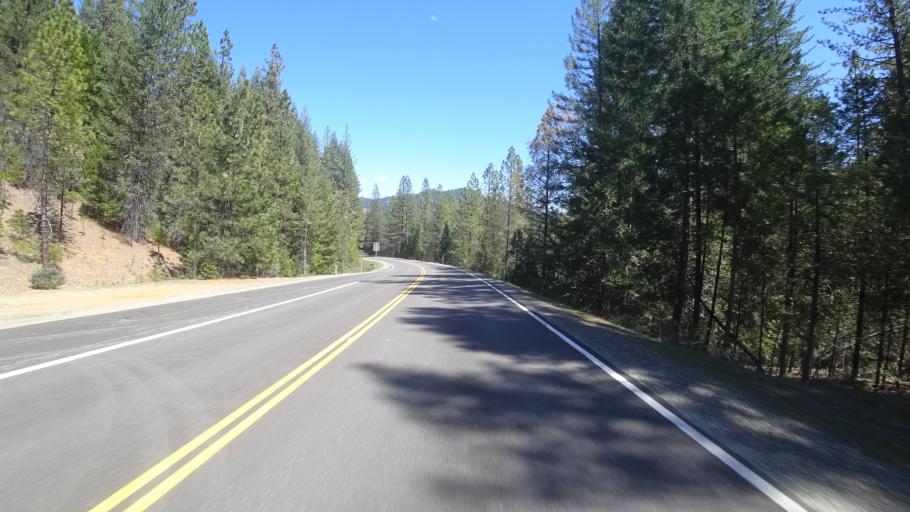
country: US
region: California
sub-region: Trinity County
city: Lewiston
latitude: 40.9051
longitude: -122.7820
